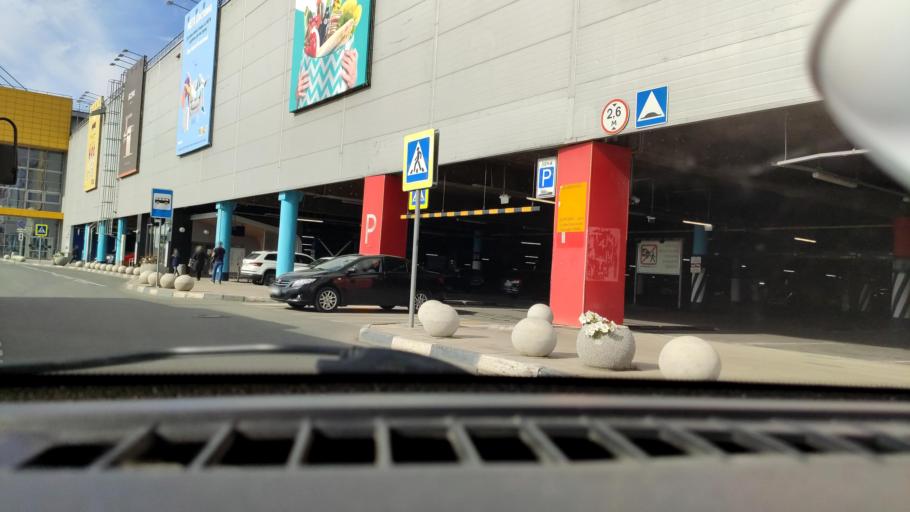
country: RU
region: Samara
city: Petra-Dubrava
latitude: 53.3250
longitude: 50.3049
